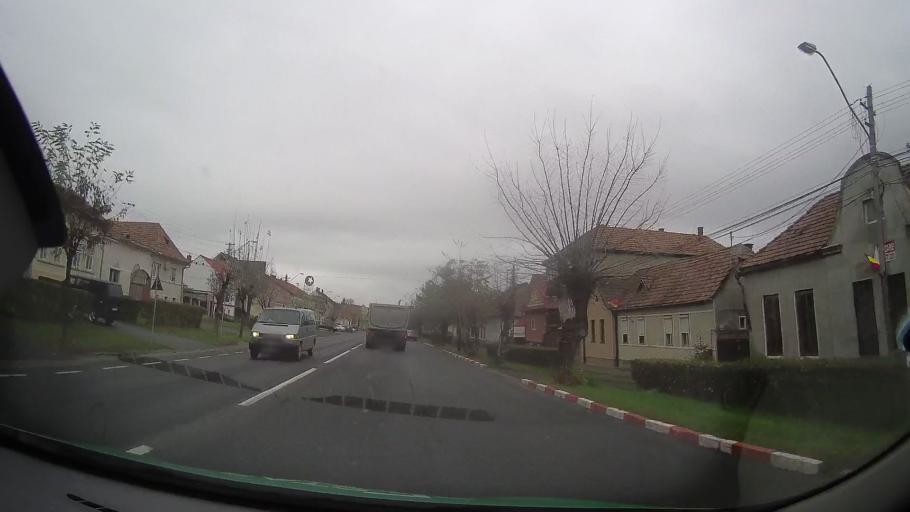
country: RO
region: Mures
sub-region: Municipiul Reghin
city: Reghin
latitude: 46.7739
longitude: 24.6928
